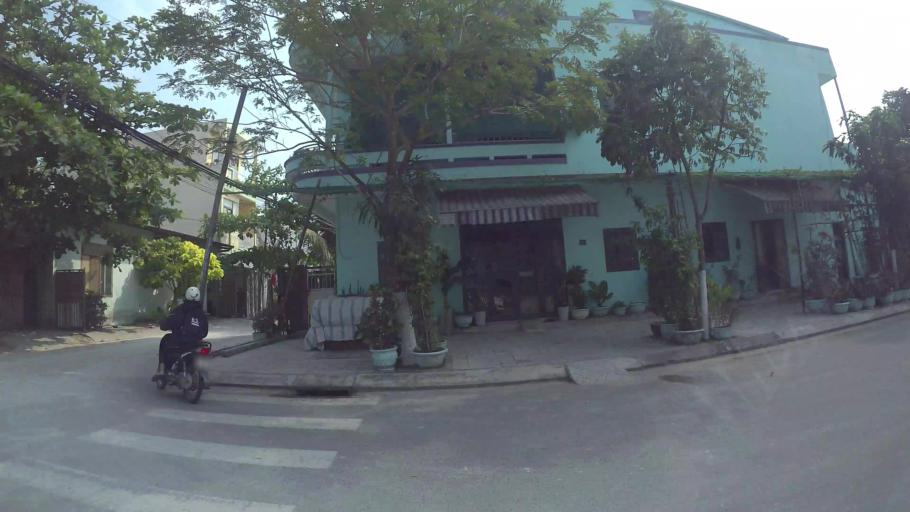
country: VN
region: Da Nang
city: Son Tra
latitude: 16.0436
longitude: 108.2429
